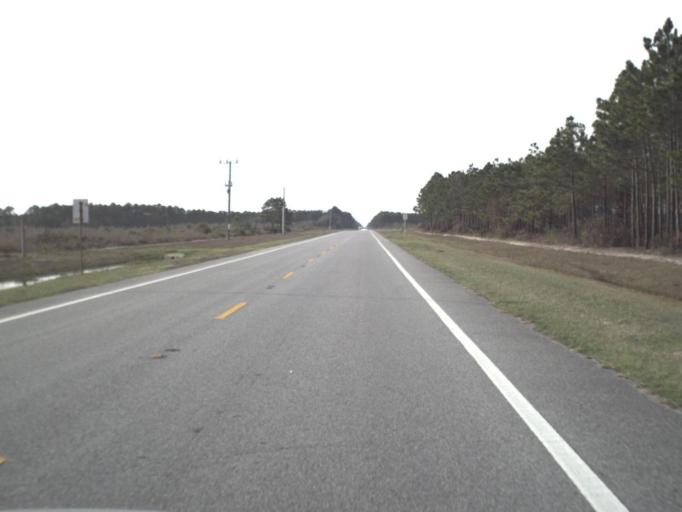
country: US
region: Florida
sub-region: Bay County
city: Tyndall Air Force Base
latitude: 30.0186
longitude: -85.5235
